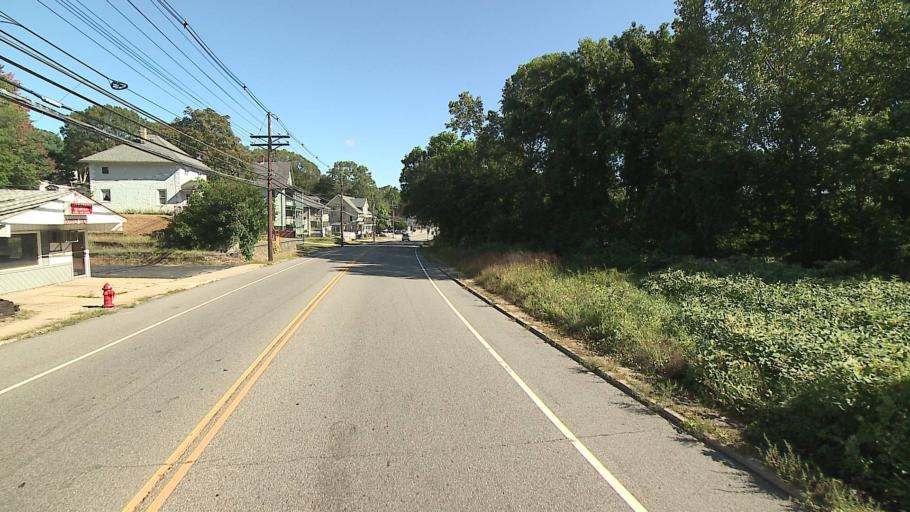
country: US
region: Connecticut
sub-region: New London County
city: Norwich
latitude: 41.5539
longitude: -72.0517
